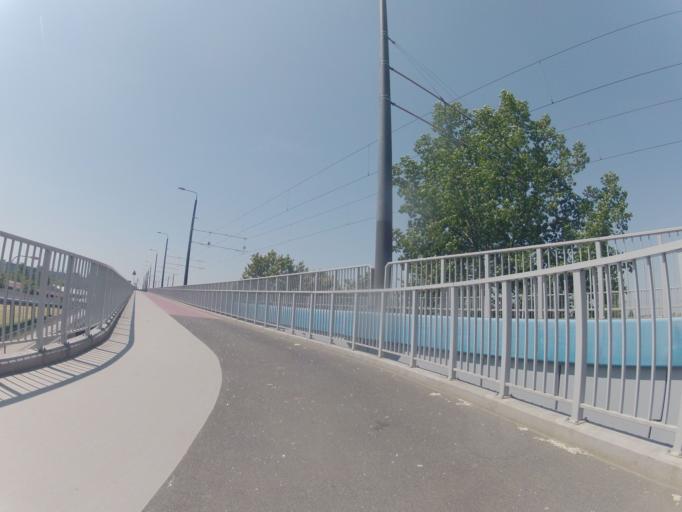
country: PL
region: Lesser Poland Voivodeship
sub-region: Krakow
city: Krakow
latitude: 50.0364
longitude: 19.9821
